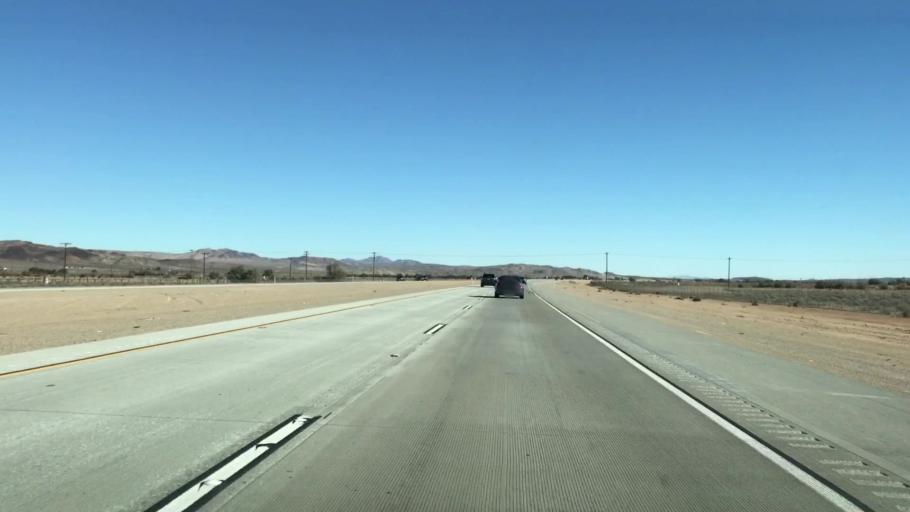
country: US
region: California
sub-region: San Bernardino County
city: Lenwood
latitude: 34.9170
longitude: -117.1758
